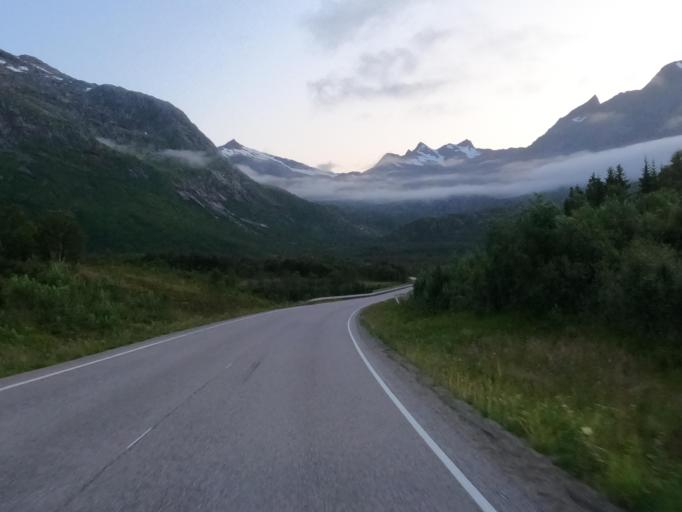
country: NO
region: Nordland
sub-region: Lodingen
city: Lodingen
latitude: 68.5286
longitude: 15.7555
